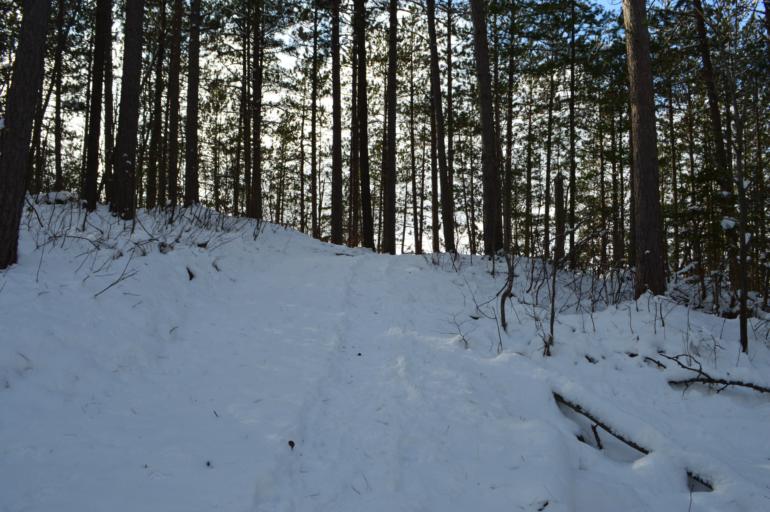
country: CA
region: Ontario
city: Bancroft
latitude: 45.5850
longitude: -78.4129
